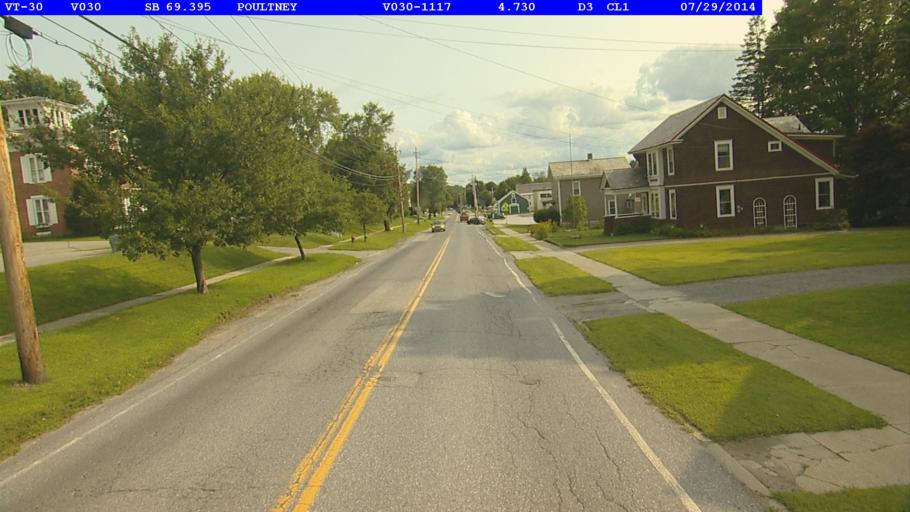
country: US
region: Vermont
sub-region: Rutland County
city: Poultney
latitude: 43.5194
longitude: -73.2327
